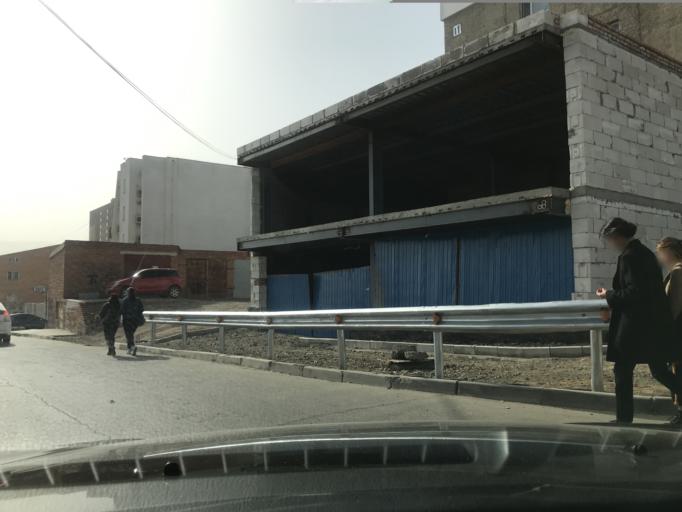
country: MN
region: Ulaanbaatar
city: Ulaanbaatar
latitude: 47.9191
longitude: 106.9523
